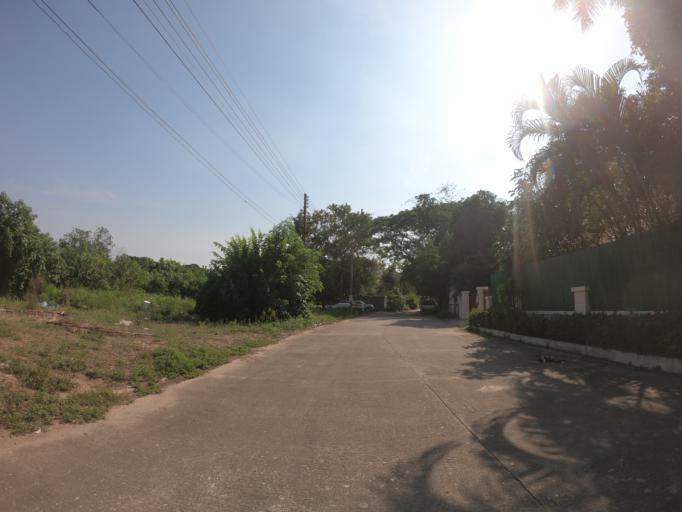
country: TH
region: Chiang Mai
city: Chiang Mai
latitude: 18.8169
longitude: 99.0080
